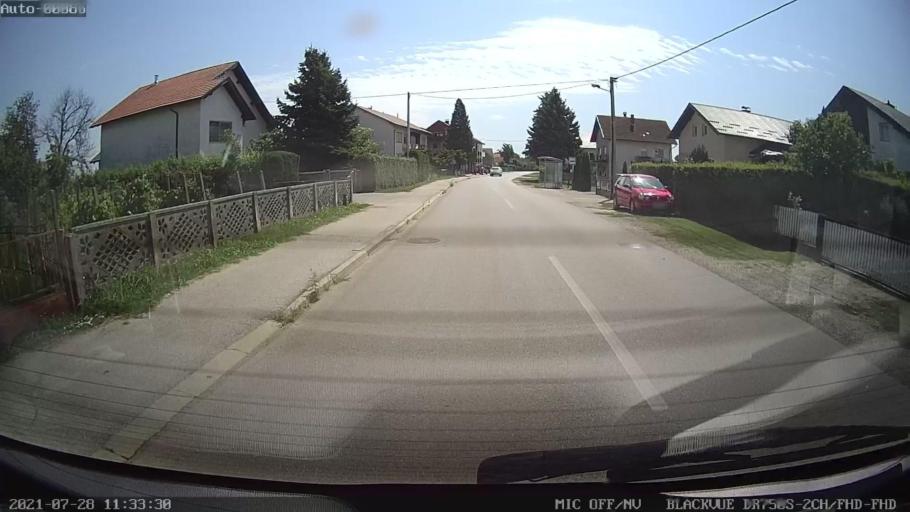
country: HR
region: Medimurska
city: Kursanec
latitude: 46.2858
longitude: 16.3842
